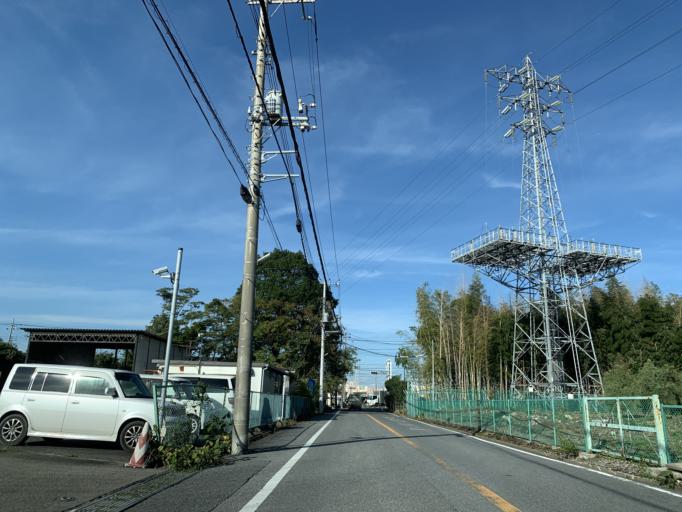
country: JP
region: Chiba
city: Nagareyama
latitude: 35.8980
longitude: 139.9295
